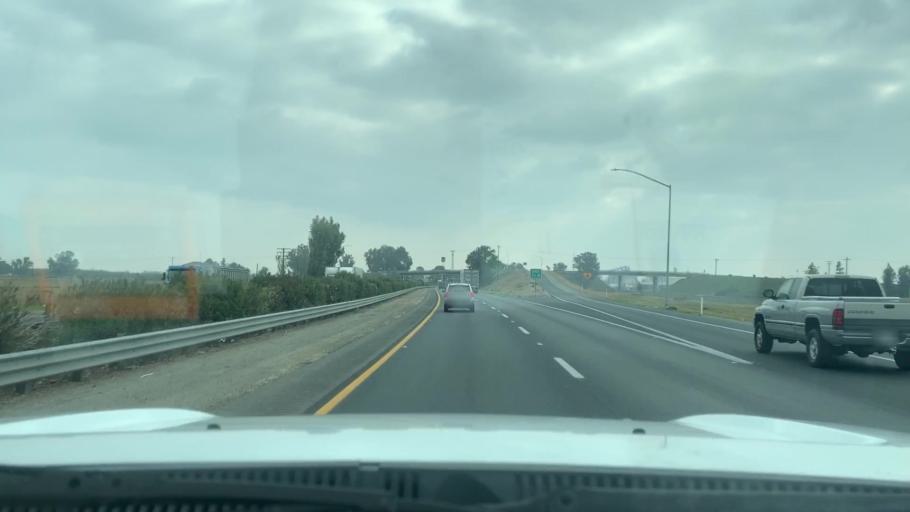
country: US
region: California
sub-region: Tulare County
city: Pixley
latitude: 36.0111
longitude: -119.3032
